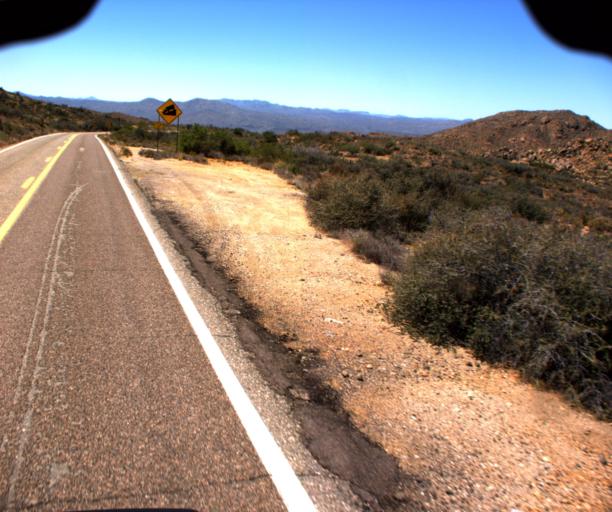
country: US
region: Arizona
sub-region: Yavapai County
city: Bagdad
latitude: 34.4436
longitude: -112.9513
